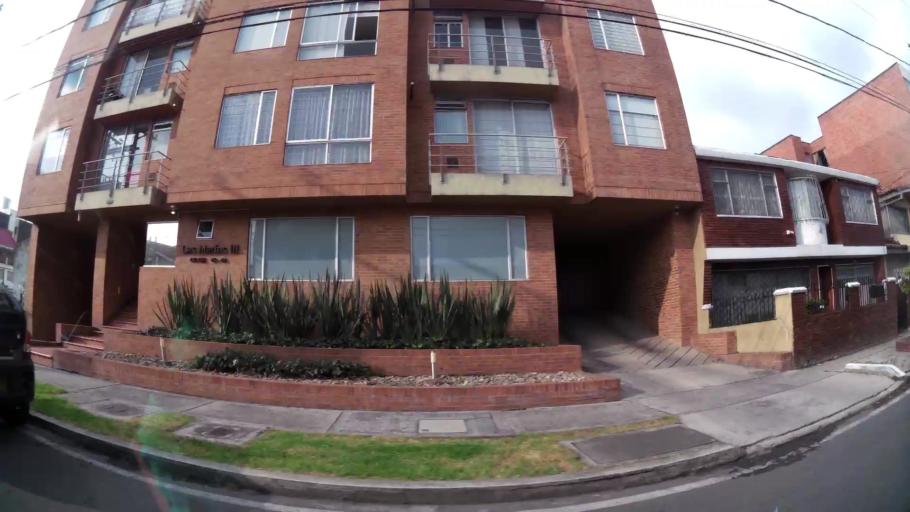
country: CO
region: Bogota D.C.
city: Barrio San Luis
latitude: 4.7216
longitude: -74.0538
